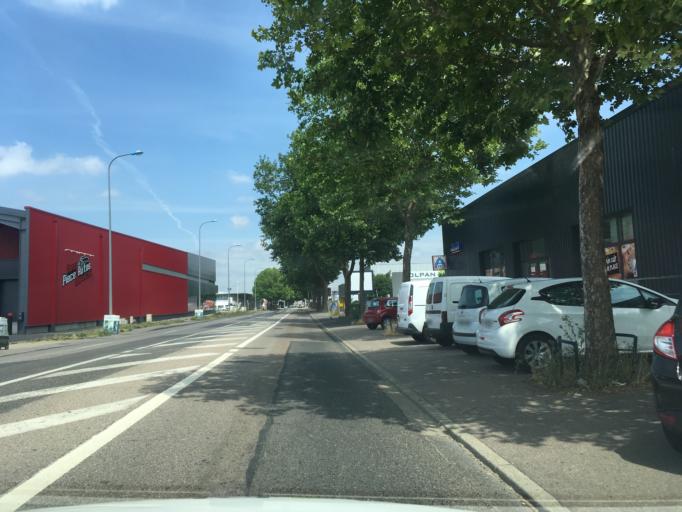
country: FR
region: Lorraine
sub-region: Departement de Meurthe-et-Moselle
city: Tomblaine
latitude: 48.6805
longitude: 6.2043
